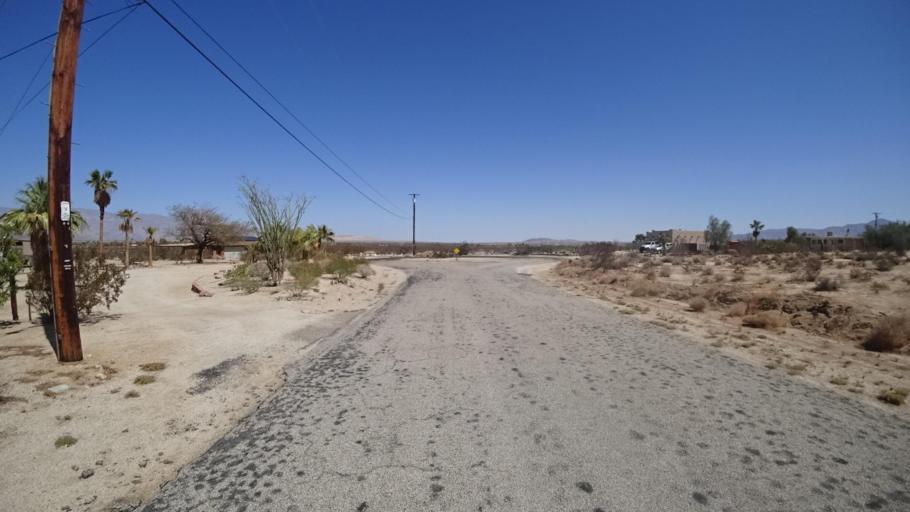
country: US
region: California
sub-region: San Diego County
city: Borrego Springs
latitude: 33.2274
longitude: -116.3667
